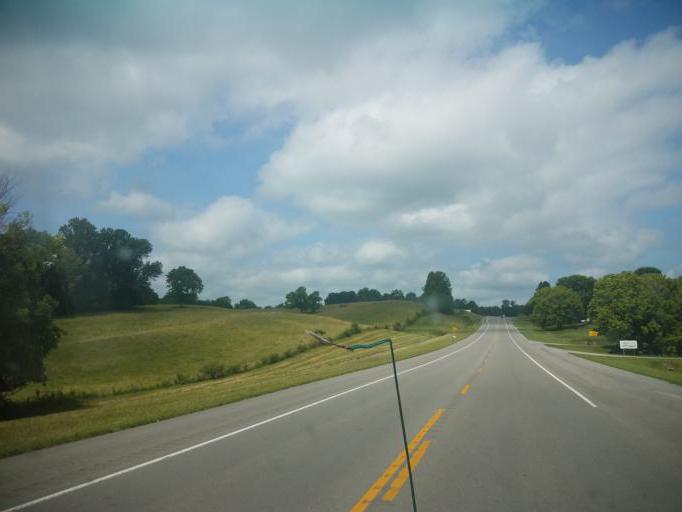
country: US
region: Kentucky
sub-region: Cumberland County
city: Burkesville
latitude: 36.7694
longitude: -85.2440
